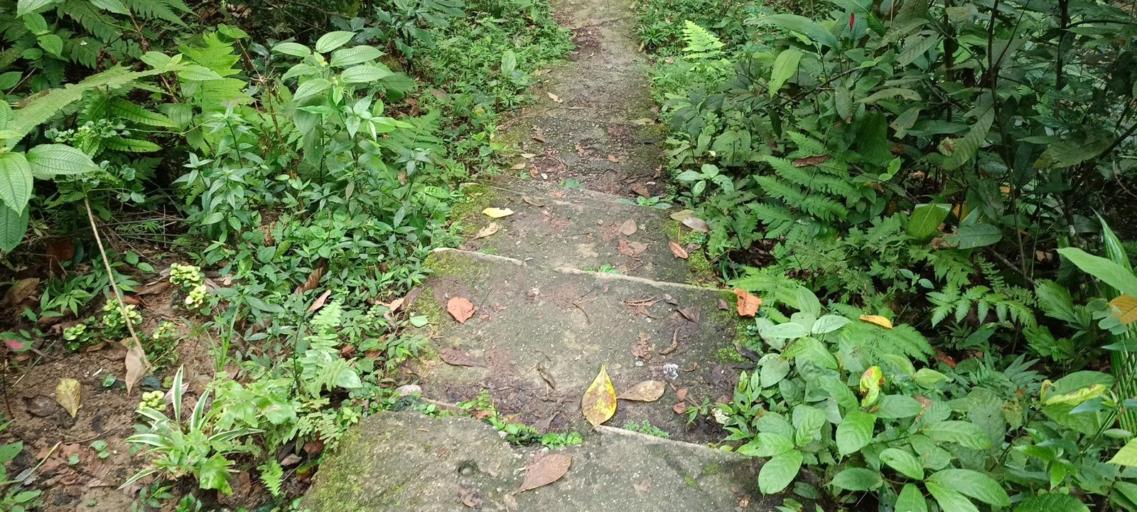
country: MY
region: Penang
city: Bukit Mertajam
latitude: 5.3615
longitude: 100.4940
